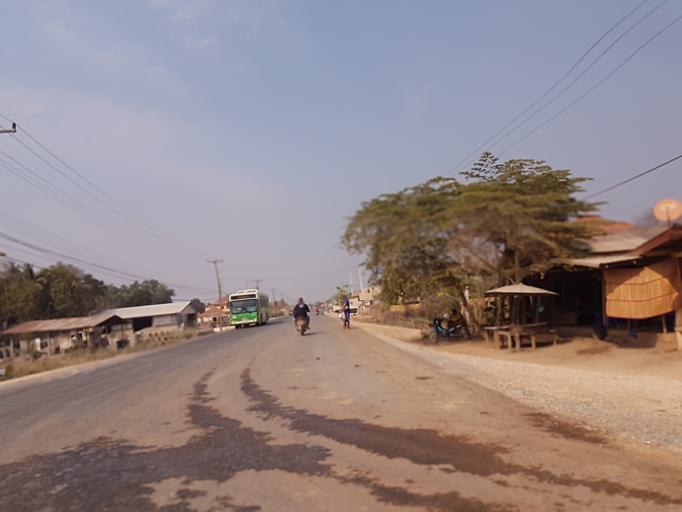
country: TH
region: Nong Khai
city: Nong Khai
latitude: 17.9173
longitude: 102.7661
